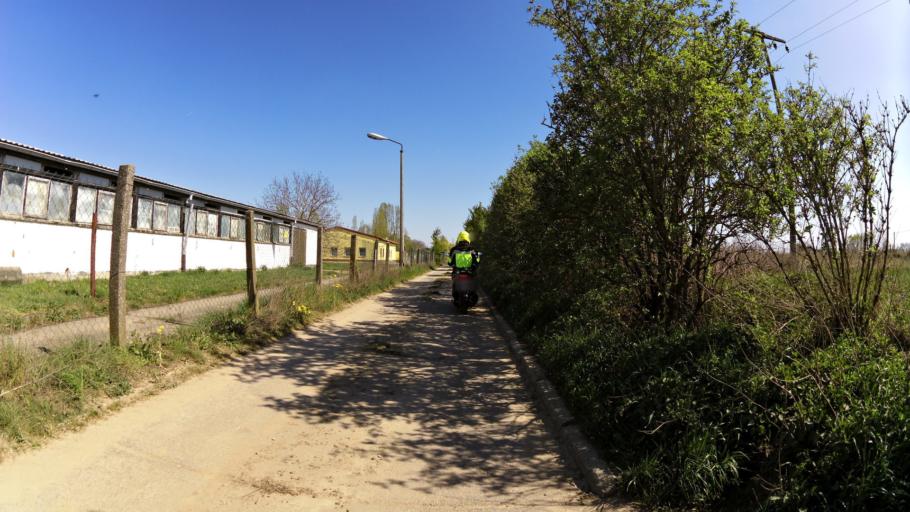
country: DE
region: Brandenburg
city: Muncheberg
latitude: 52.5204
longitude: 14.1454
